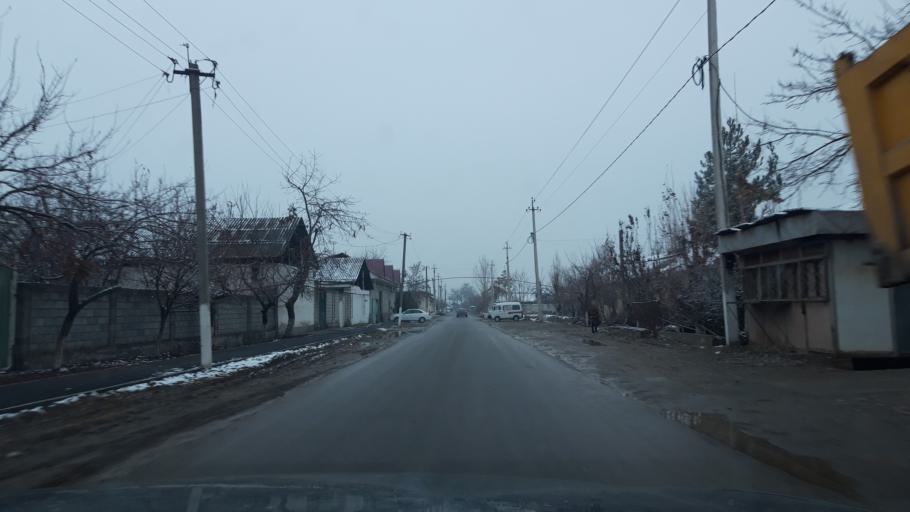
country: UZ
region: Andijon
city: Andijon
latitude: 40.7408
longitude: 72.2570
